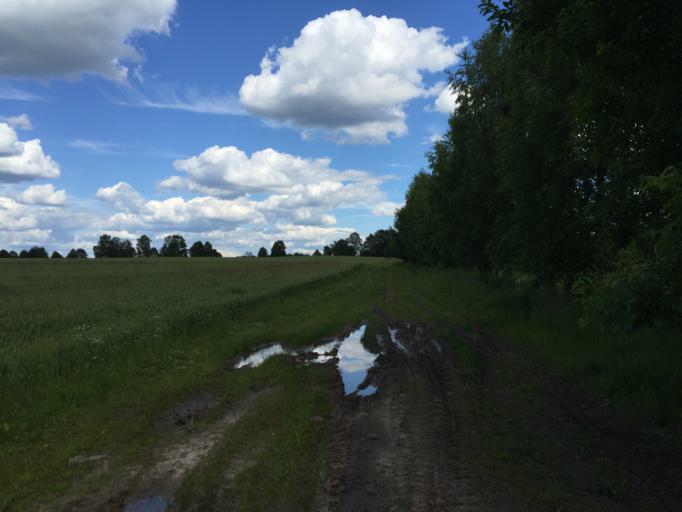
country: LV
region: Sigulda
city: Sigulda
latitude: 57.1690
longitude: 24.8826
